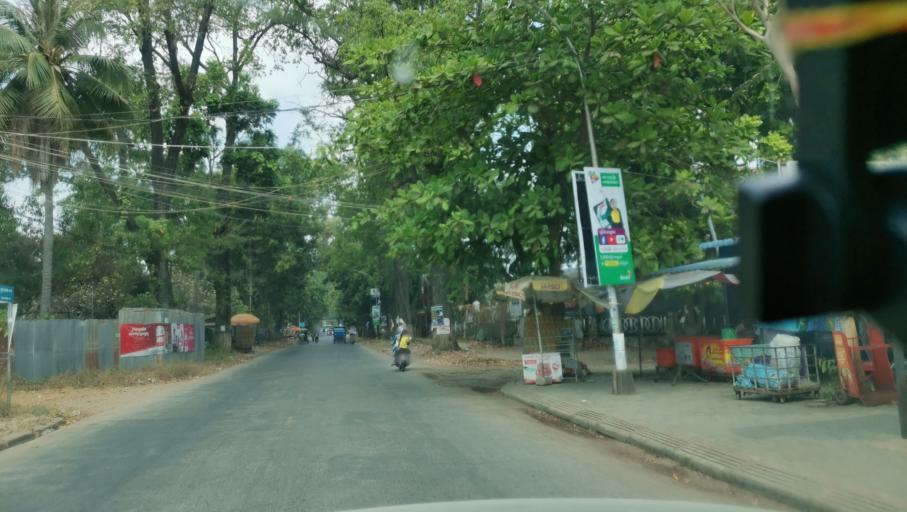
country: KH
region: Battambang
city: Battambang
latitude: 13.0880
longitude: 103.2003
